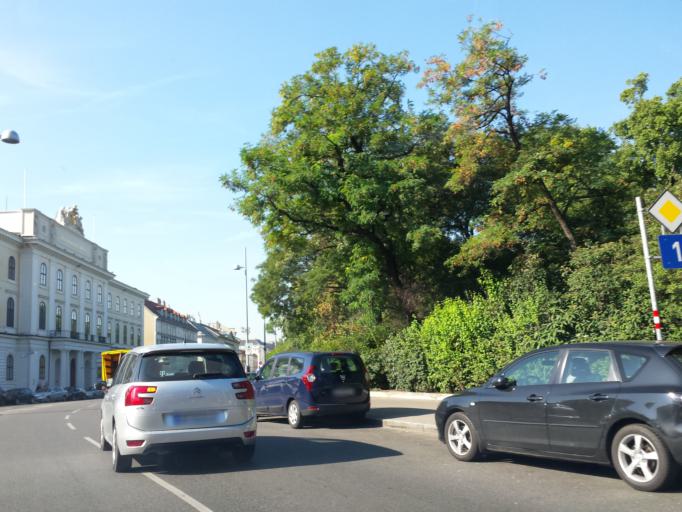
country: AT
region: Vienna
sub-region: Wien Stadt
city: Vienna
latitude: 48.2044
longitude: 16.3831
